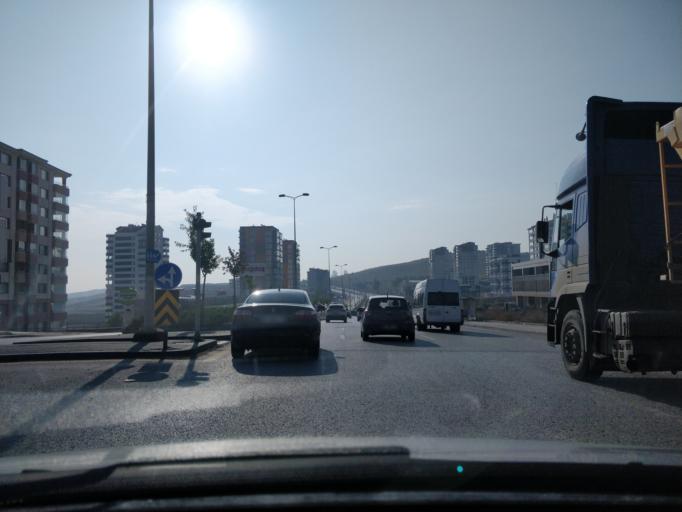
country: TR
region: Ankara
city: Etimesgut
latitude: 39.8972
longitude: 32.6521
